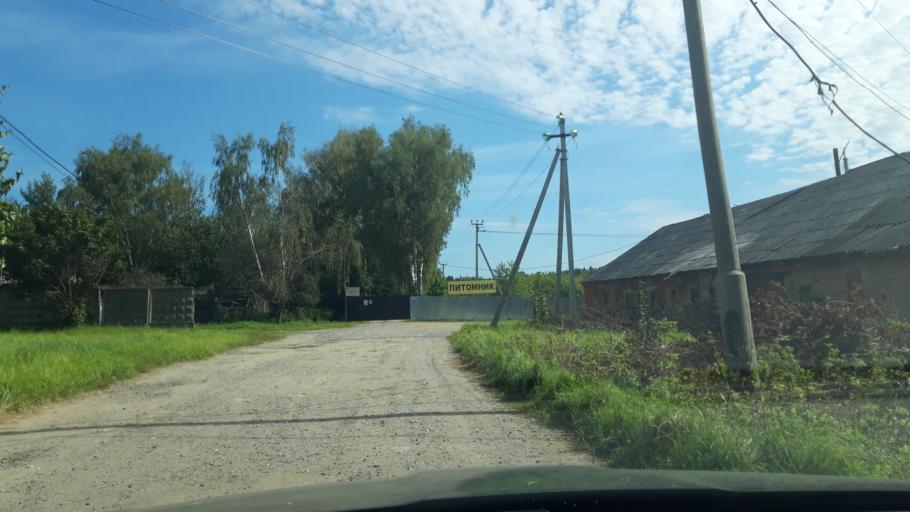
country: RU
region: Moskovskaya
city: Chashnikovo
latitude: 56.0342
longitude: 37.1702
